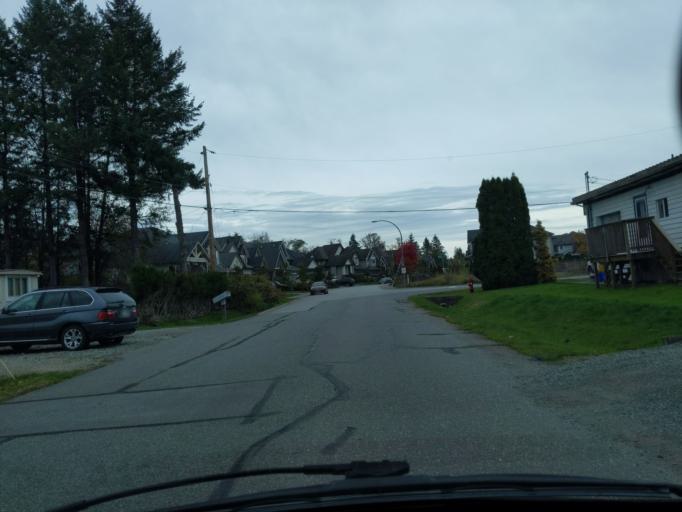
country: CA
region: British Columbia
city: Walnut Grove
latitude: 49.1827
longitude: -122.6607
